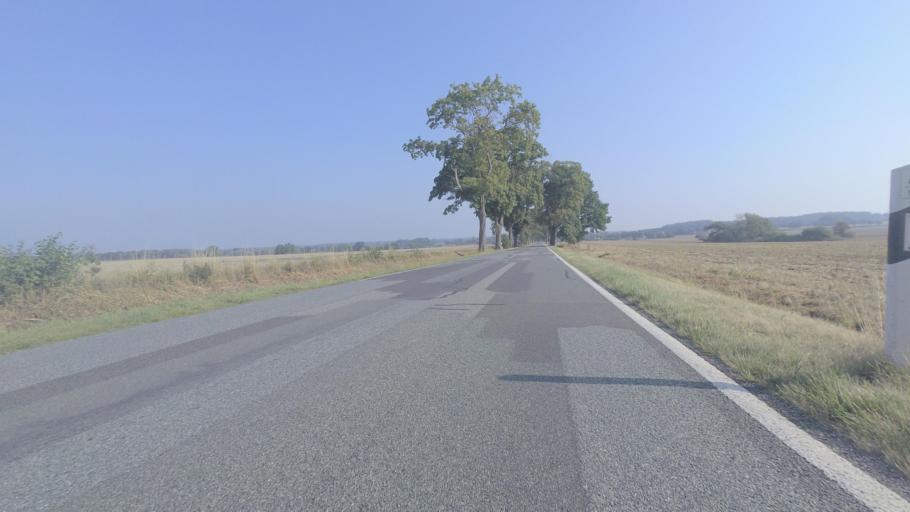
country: DE
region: Mecklenburg-Vorpommern
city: Malchow
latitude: 53.3778
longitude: 12.3888
